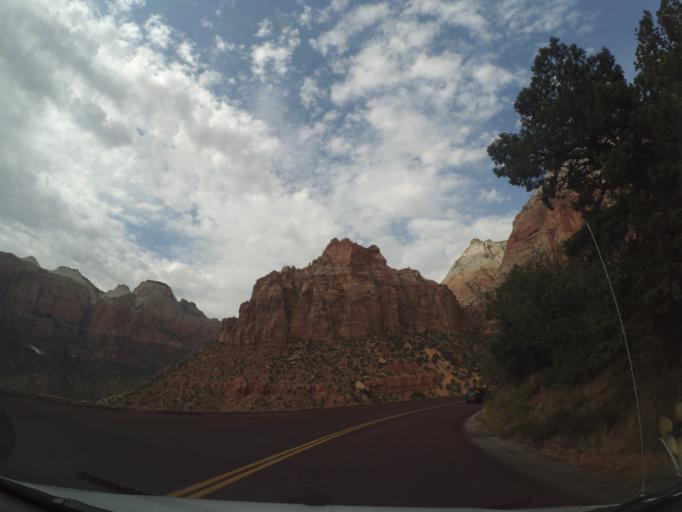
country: US
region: Utah
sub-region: Washington County
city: Hildale
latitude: 37.2138
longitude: -112.9636
